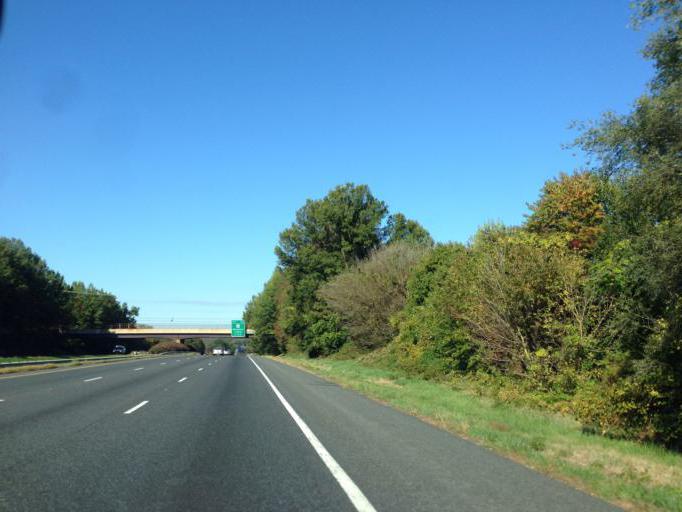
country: US
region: Maryland
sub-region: Carroll County
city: Sykesville
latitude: 39.3372
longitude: -77.0465
